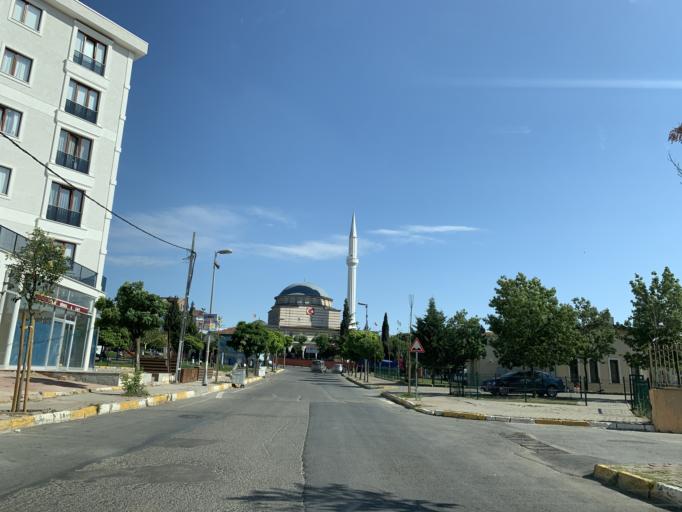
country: TR
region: Istanbul
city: Pendik
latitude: 40.8816
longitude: 29.2803
